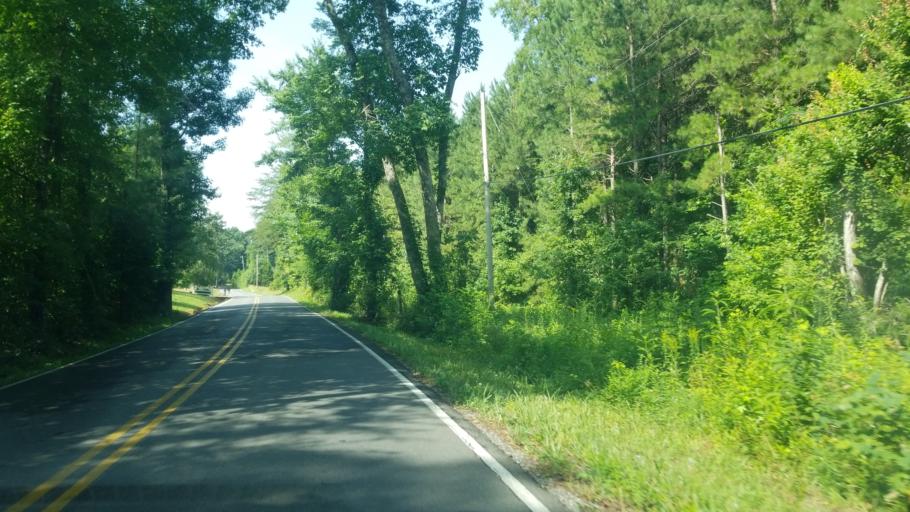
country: US
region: Tennessee
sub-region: Hamilton County
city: Collegedale
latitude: 35.0806
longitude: -84.9958
